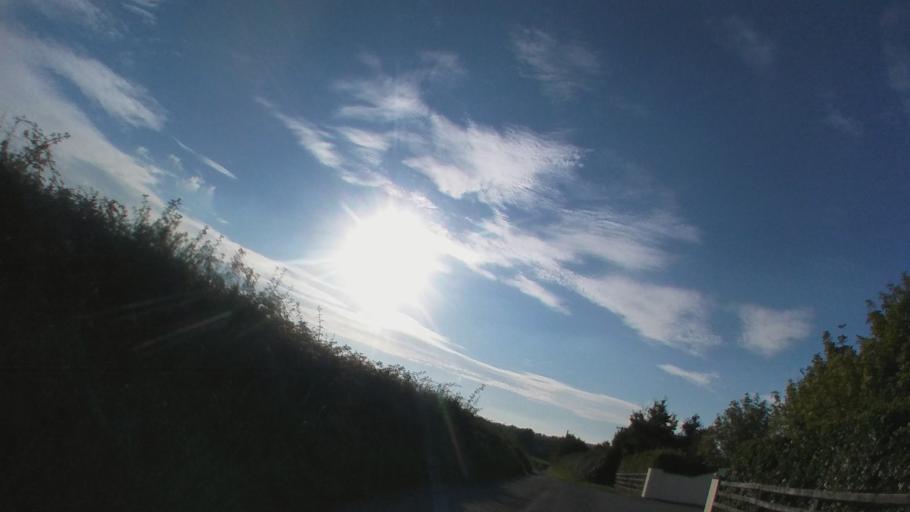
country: IE
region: Leinster
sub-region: Kilkenny
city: Kilkenny
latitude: 52.6959
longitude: -7.1952
